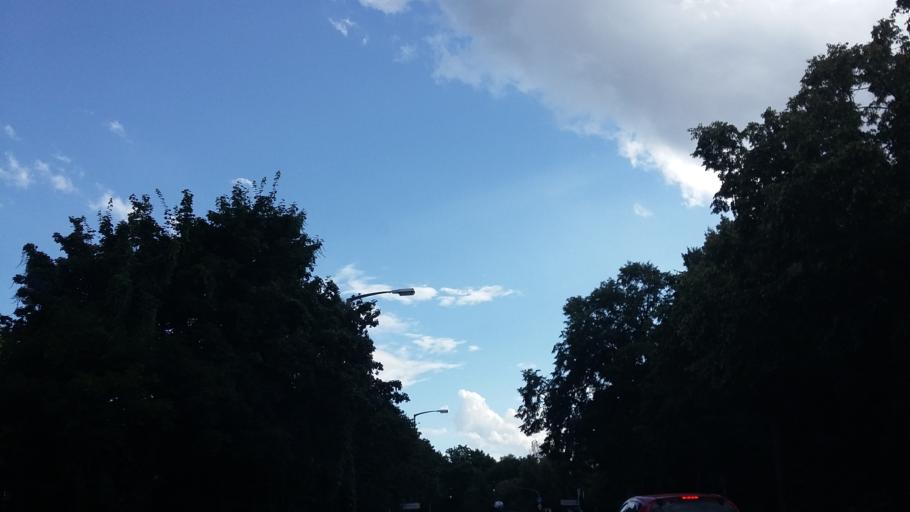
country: DE
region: Bavaria
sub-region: Swabia
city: Augsburg
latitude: 48.3869
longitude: 10.9081
